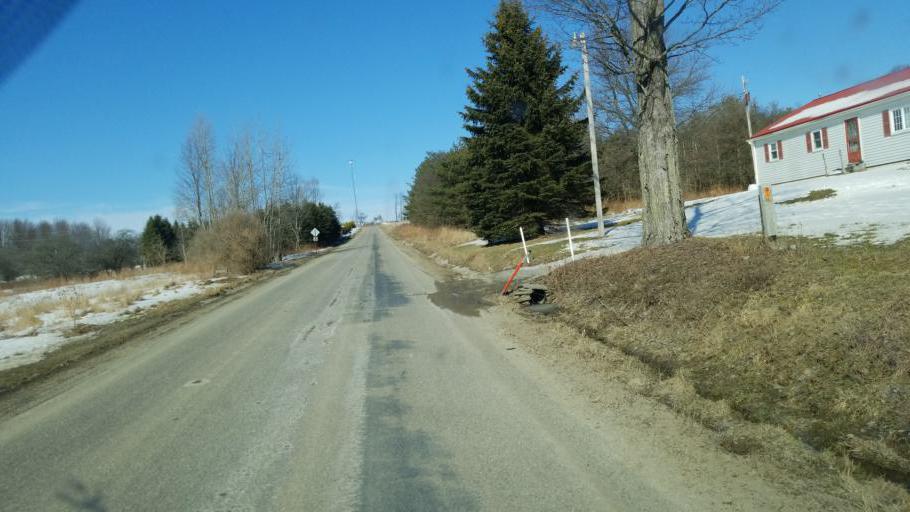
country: US
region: Pennsylvania
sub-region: Tioga County
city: Westfield
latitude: 41.9909
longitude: -77.6742
